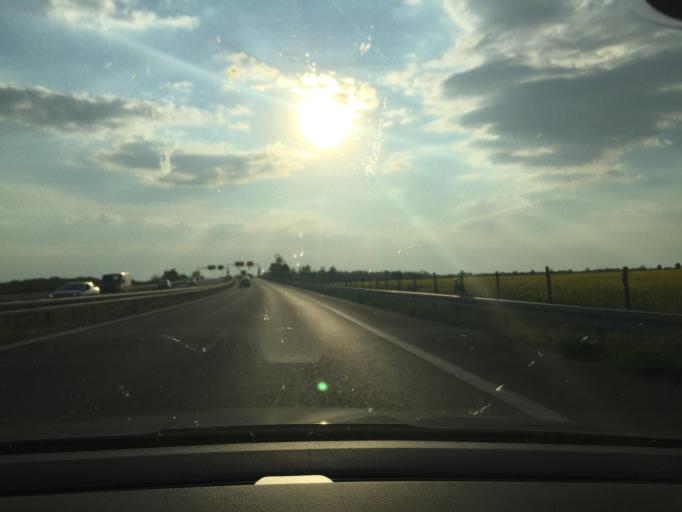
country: DE
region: Berlin
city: Lichtenrade
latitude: 52.3668
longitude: 13.4313
